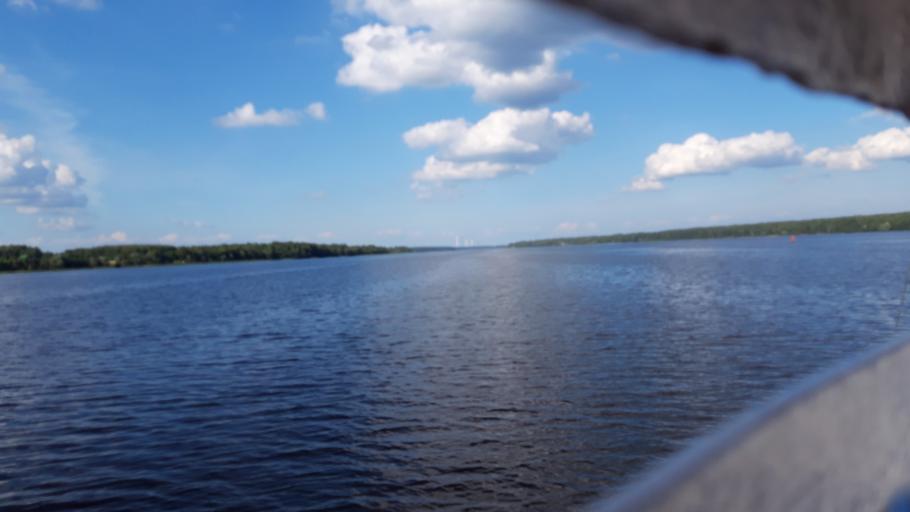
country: RU
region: Tverskaya
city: Konakovo
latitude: 56.6667
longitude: 36.6581
